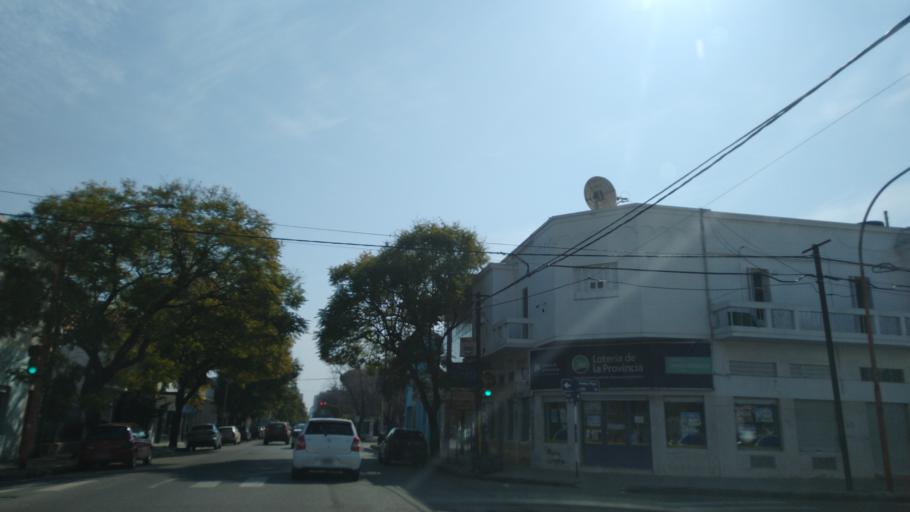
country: AR
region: Buenos Aires
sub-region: Partido de Bahia Blanca
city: Bahia Blanca
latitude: -38.7285
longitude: -62.2570
